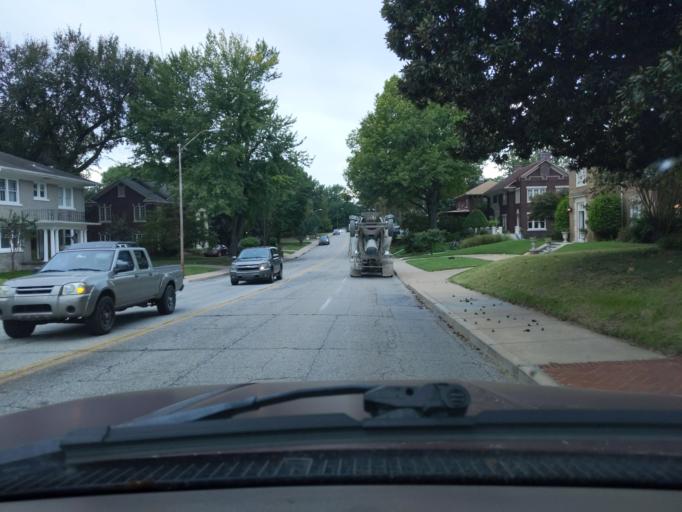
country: US
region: Oklahoma
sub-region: Tulsa County
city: Tulsa
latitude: 36.1334
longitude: -95.9775
